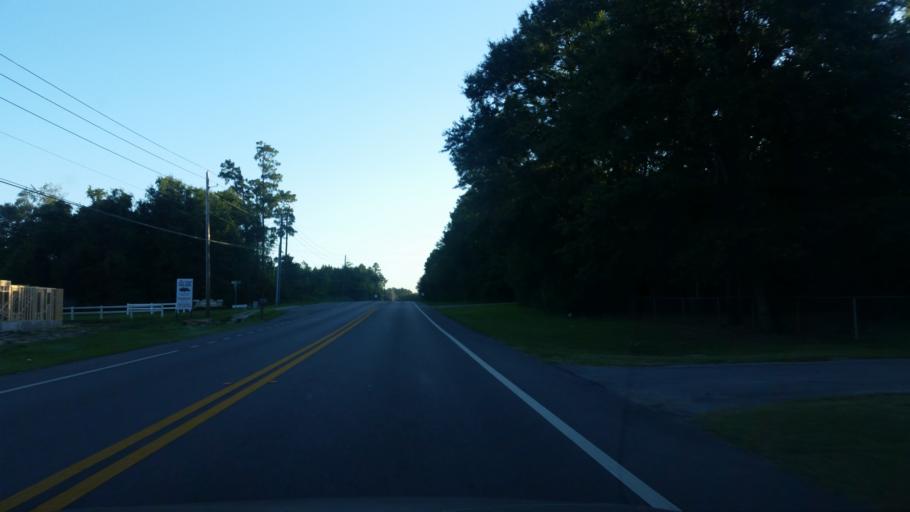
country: US
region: Florida
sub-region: Escambia County
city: Cantonment
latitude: 30.5915
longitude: -87.3281
